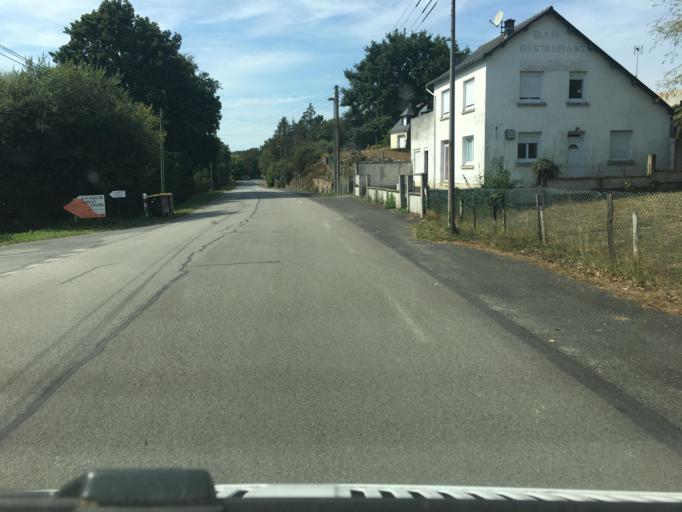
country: FR
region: Brittany
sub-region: Departement des Cotes-d'Armor
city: Mur-de-Bretagne
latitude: 48.1978
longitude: -3.0096
